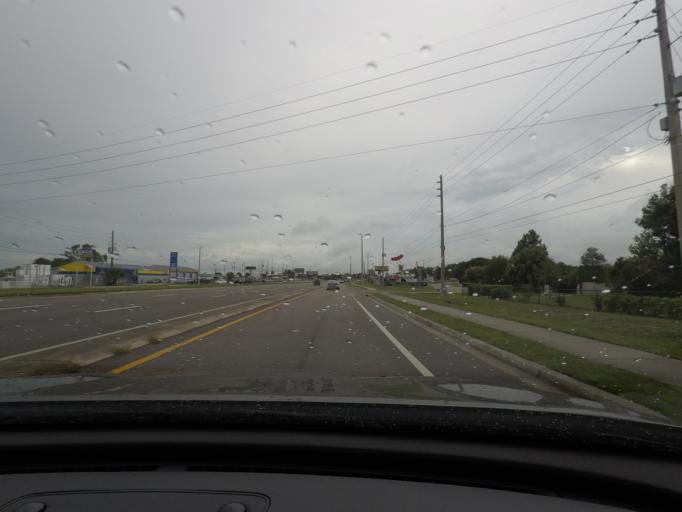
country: US
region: Florida
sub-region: Orange County
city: Azalea Park
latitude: 28.5555
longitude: -81.3144
